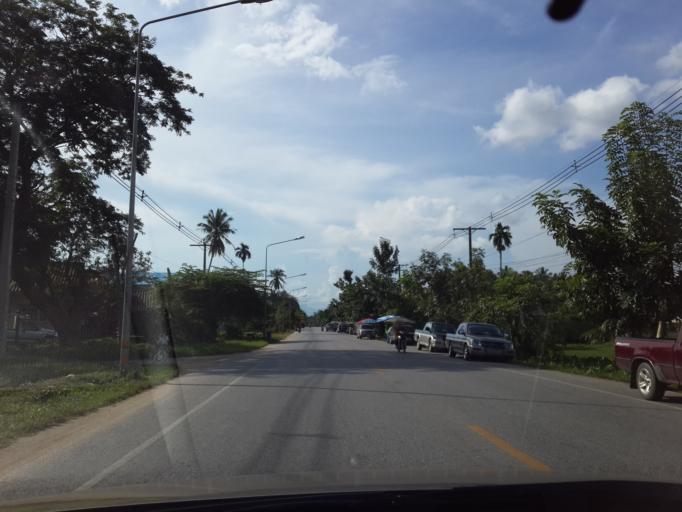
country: TH
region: Yala
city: Yala
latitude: 6.4906
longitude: 101.3071
